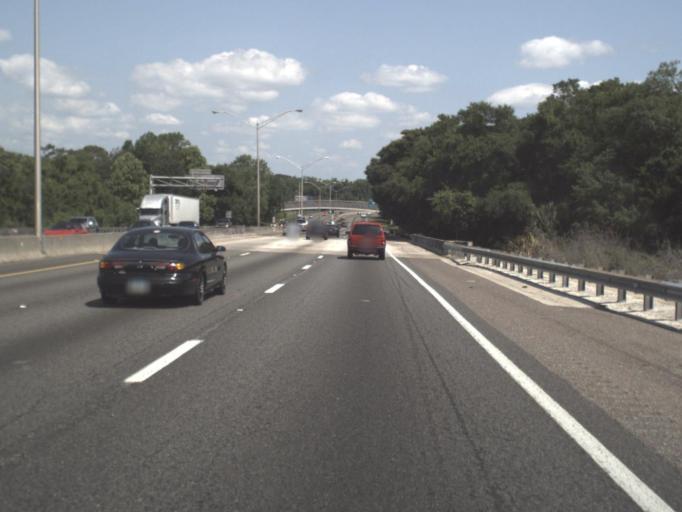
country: US
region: Florida
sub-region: Duval County
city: Jacksonville
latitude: 30.3742
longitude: -81.6700
